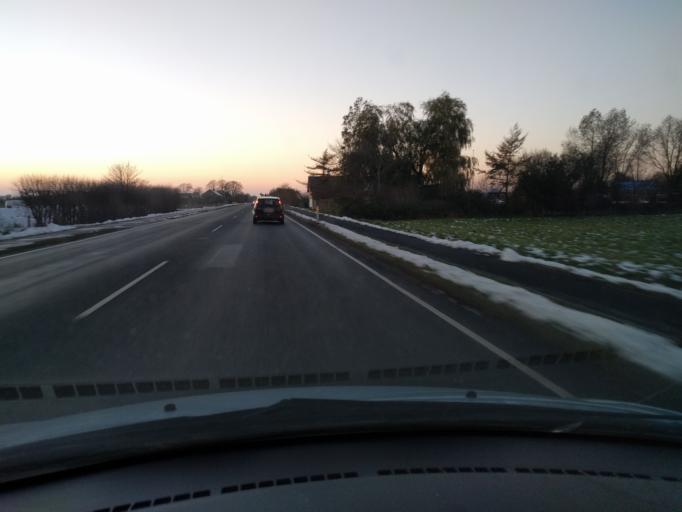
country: DK
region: South Denmark
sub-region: Nyborg Kommune
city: Ullerslev
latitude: 55.3595
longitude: 10.6933
